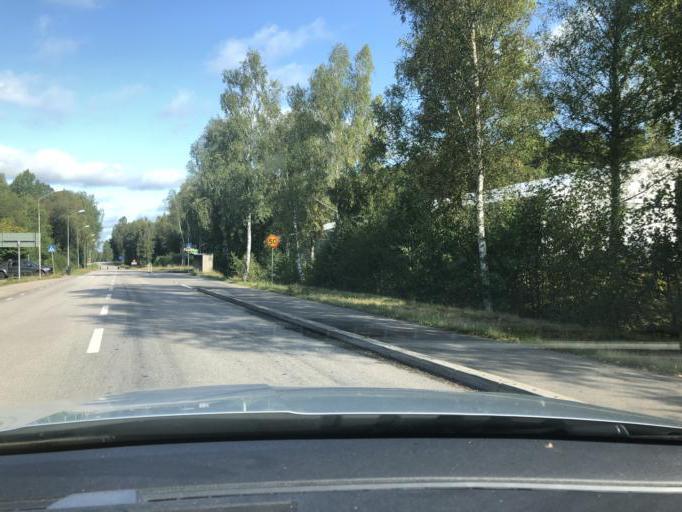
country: SE
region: Blekinge
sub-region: Karlshamns Kommun
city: Svangsta
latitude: 56.4085
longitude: 14.6604
